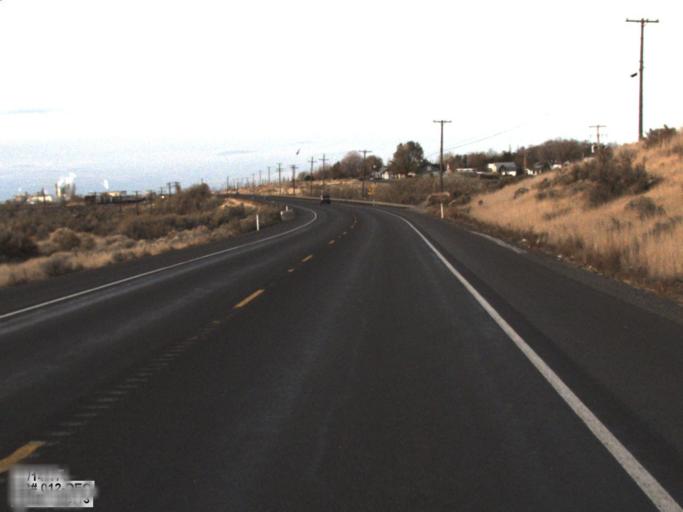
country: US
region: Washington
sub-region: Benton County
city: Finley
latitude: 46.0773
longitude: -118.9077
